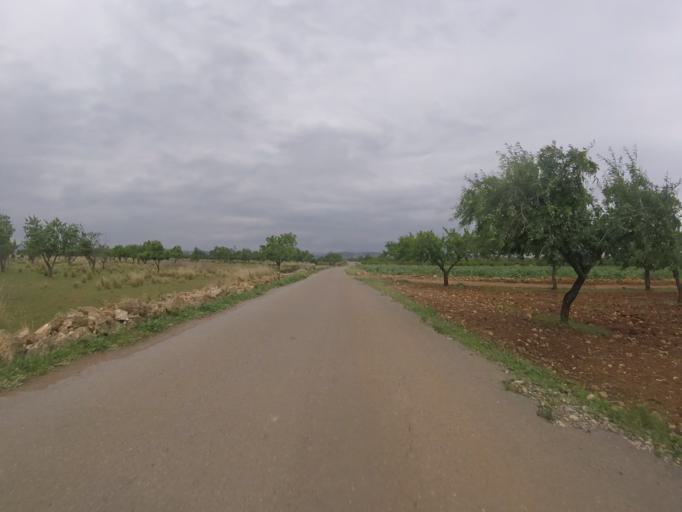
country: ES
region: Valencia
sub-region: Provincia de Castello
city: Torreblanca
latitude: 40.2149
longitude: 0.2361
